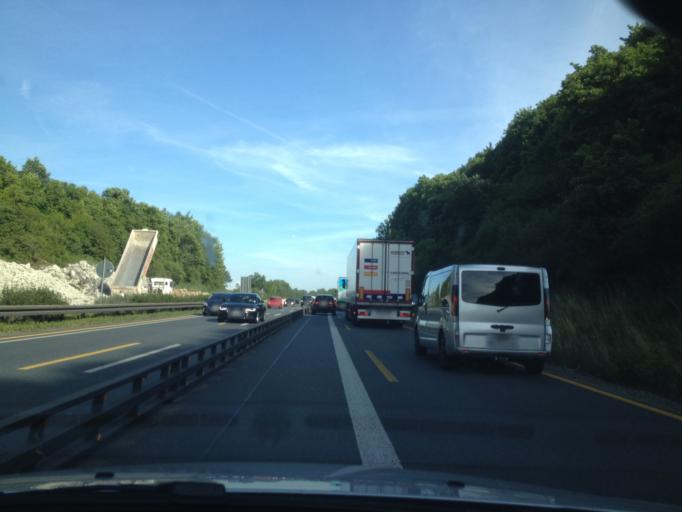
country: DE
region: Hesse
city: Allendorf an der Lahn
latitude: 50.5443
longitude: 8.5732
